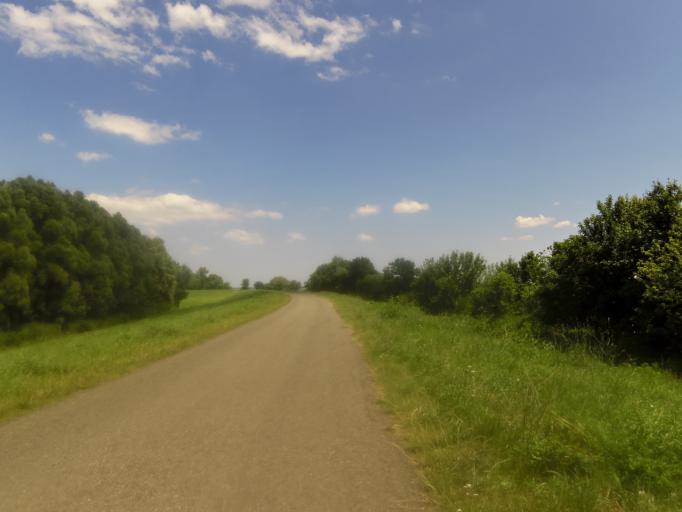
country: HU
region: Heves
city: Tiszanana
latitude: 47.5448
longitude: 20.6044
